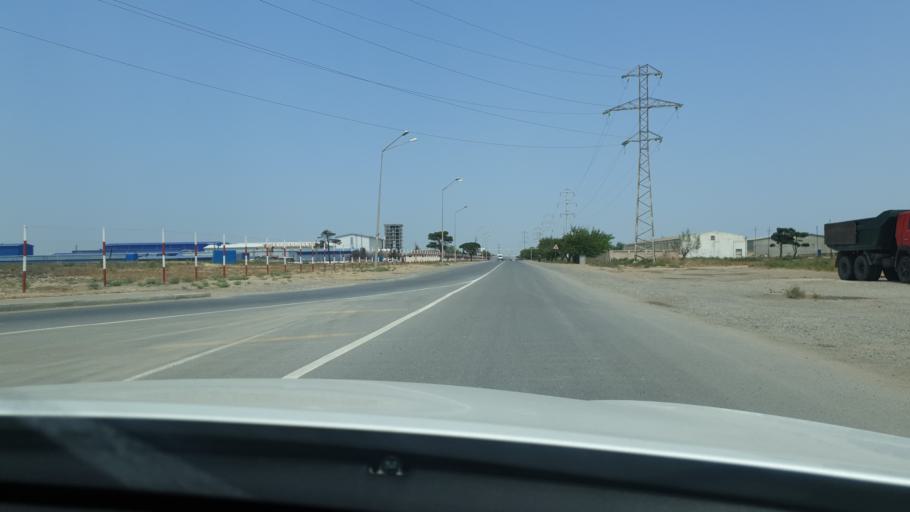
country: AZ
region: Baki
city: Qaracuxur
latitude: 40.3960
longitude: 49.9987
